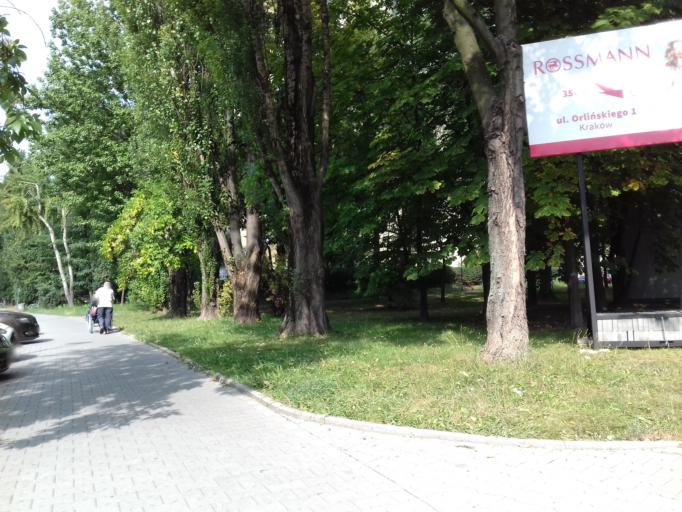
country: PL
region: Lesser Poland Voivodeship
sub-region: Krakow
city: Krakow
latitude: 50.0843
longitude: 20.0013
